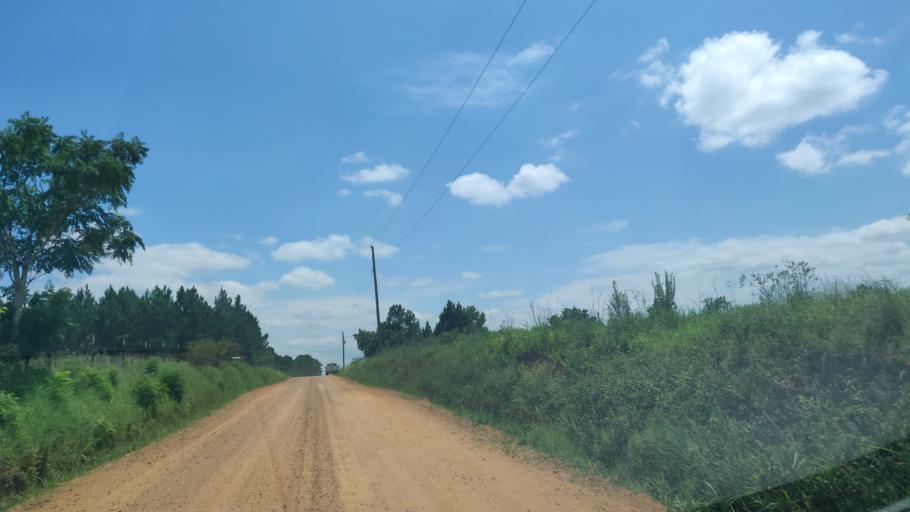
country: US
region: Georgia
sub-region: Tift County
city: Tifton
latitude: 31.4687
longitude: -83.6373
